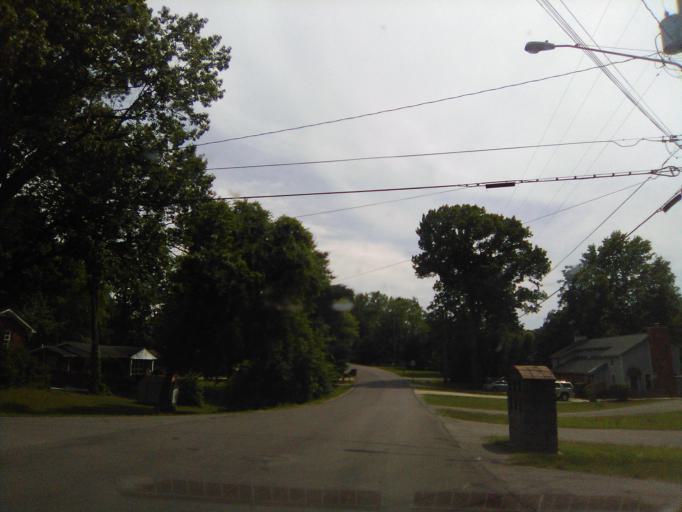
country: US
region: Tennessee
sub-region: Davidson County
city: Belle Meade
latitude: 36.1267
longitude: -86.9012
